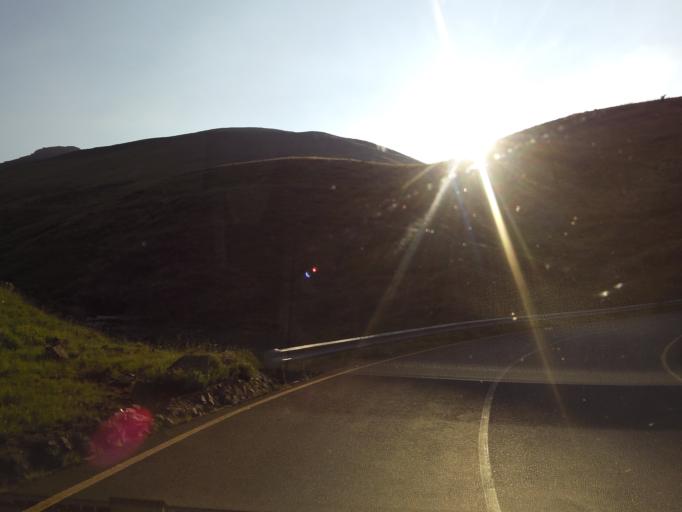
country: LS
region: Butha-Buthe
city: Butha-Buthe
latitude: -29.1132
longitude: 28.4558
